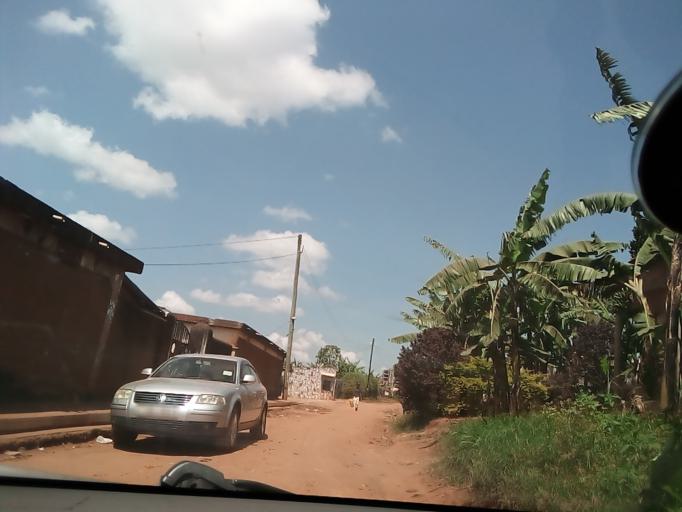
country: UG
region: Central Region
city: Masaka
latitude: -0.3366
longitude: 31.7420
